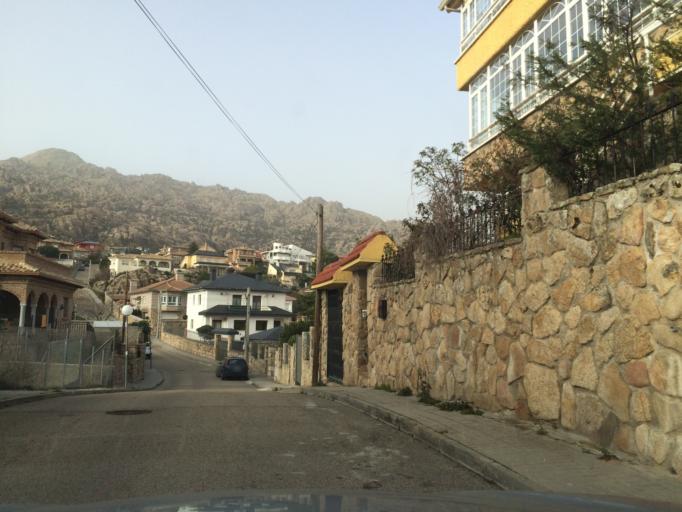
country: ES
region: Madrid
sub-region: Provincia de Madrid
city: Manzanares el Real
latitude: 40.7333
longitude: -3.8623
